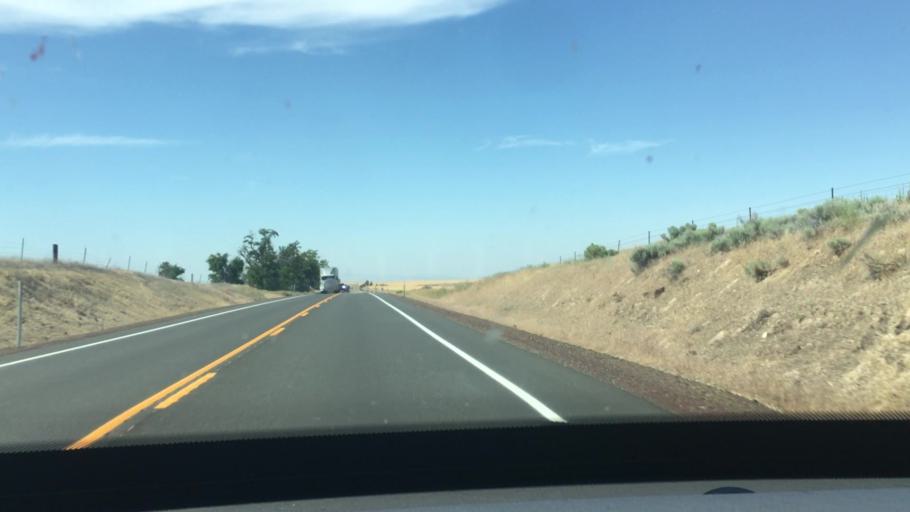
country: US
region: Oregon
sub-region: Sherman County
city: Moro
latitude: 45.3164
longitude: -120.7686
